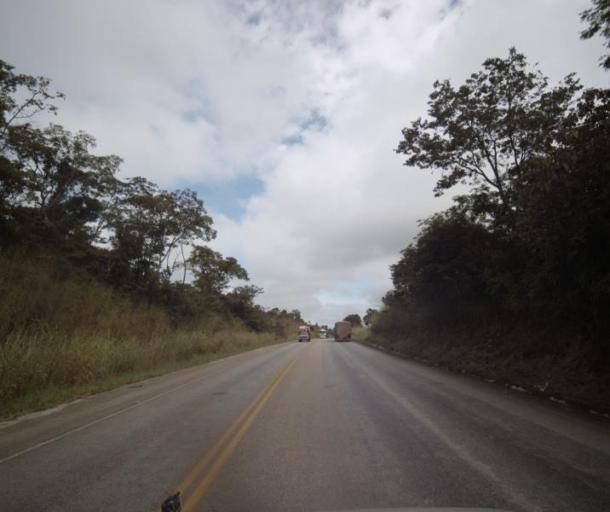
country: BR
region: Goias
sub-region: Pirenopolis
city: Pirenopolis
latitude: -15.7538
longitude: -48.7326
